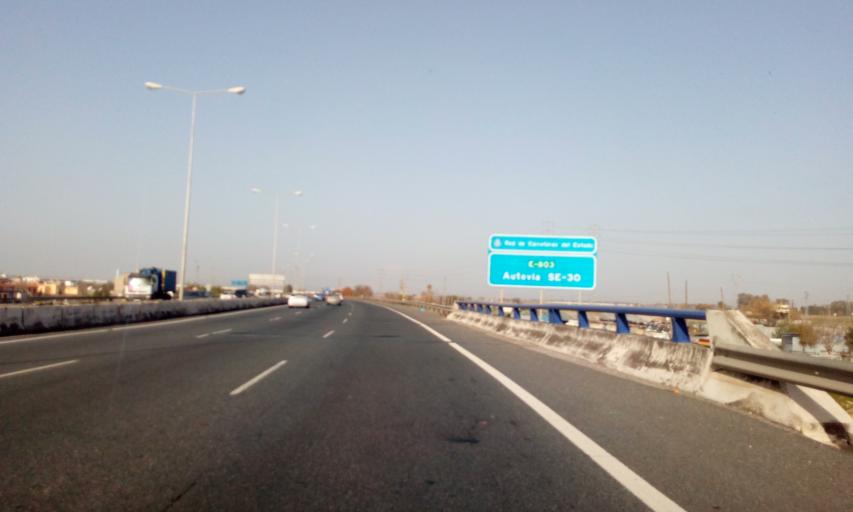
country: ES
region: Andalusia
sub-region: Provincia de Sevilla
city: Camas
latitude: 37.3942
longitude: -6.0253
